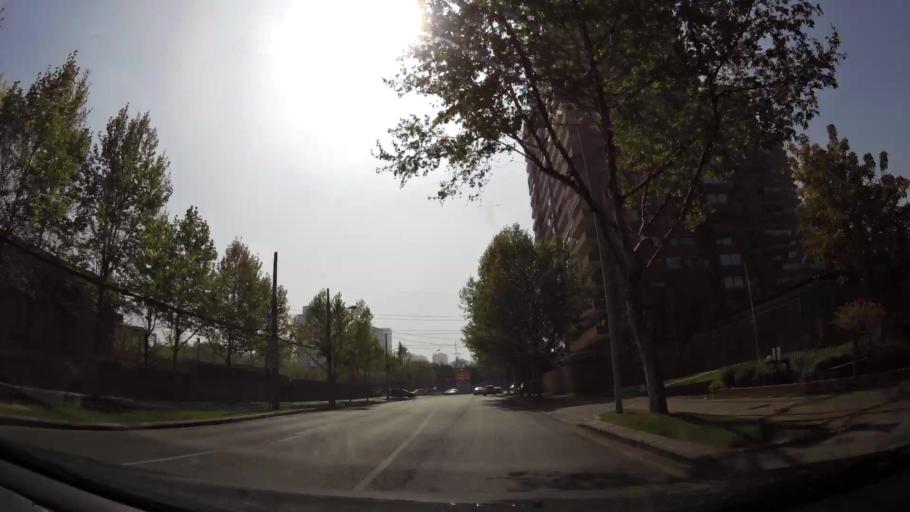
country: CL
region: Santiago Metropolitan
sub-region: Provincia de Santiago
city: Villa Presidente Frei, Nunoa, Santiago, Chile
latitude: -33.4062
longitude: -70.5801
